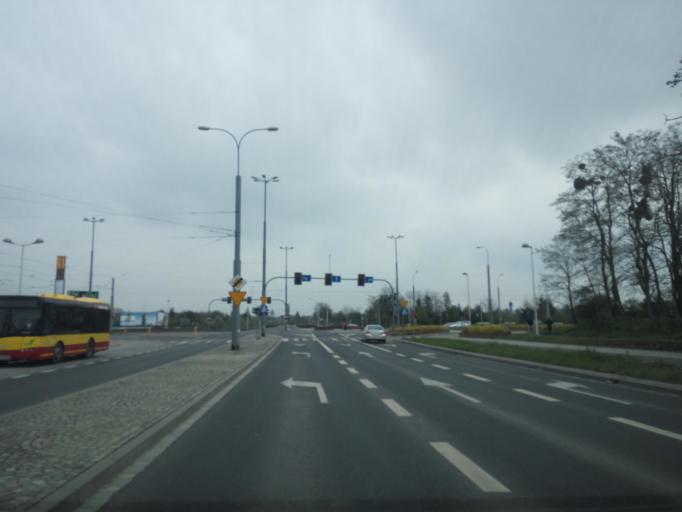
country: PL
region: Lower Silesian Voivodeship
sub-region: Powiat wroclawski
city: Wroclaw
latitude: 51.0767
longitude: 17.0506
